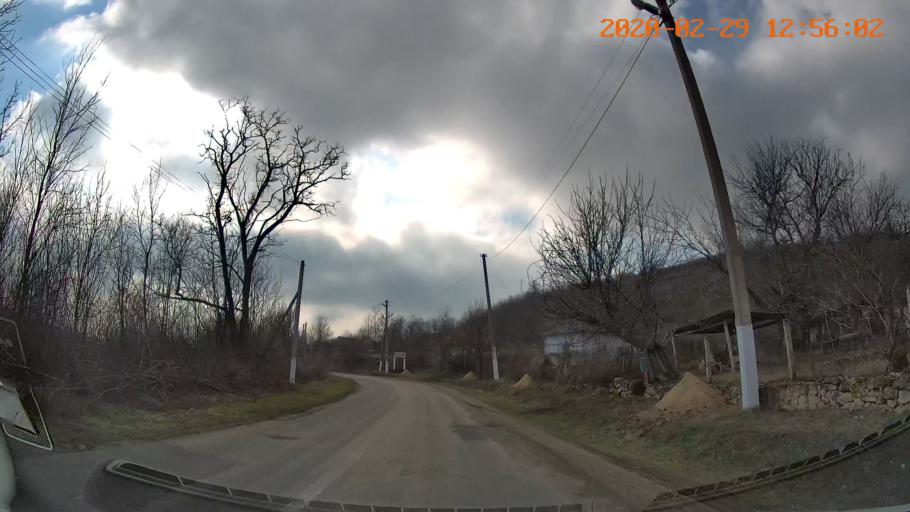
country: MD
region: Telenesti
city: Camenca
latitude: 48.0904
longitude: 28.7237
